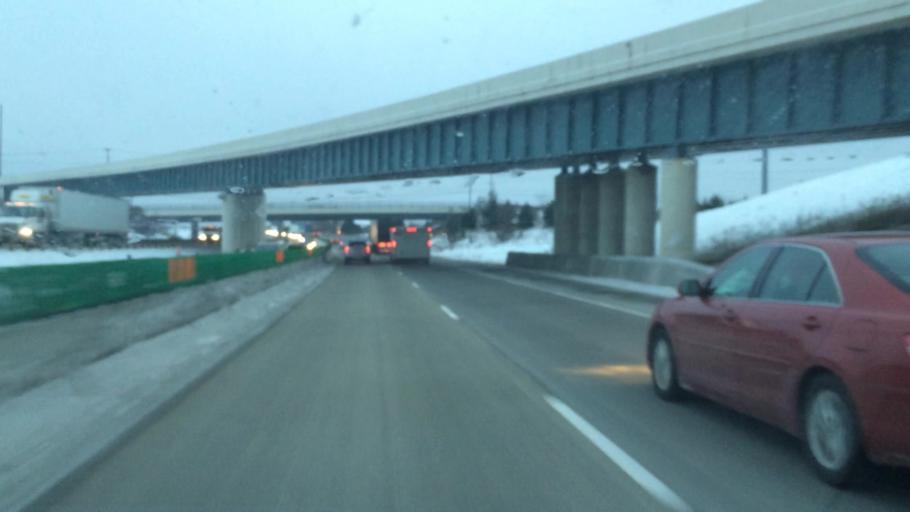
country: US
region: Ohio
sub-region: Cuyahoga County
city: Bedford Heights
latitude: 41.4072
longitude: -81.5062
